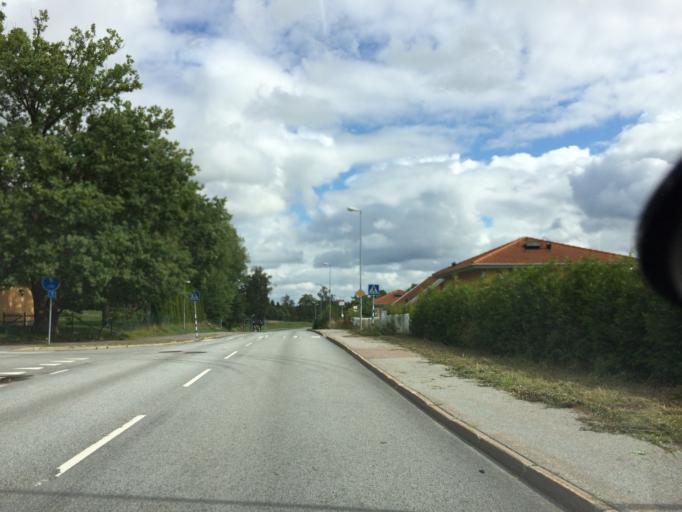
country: SE
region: Stockholm
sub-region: Upplands Vasby Kommun
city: Upplands Vaesby
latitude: 59.4618
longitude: 17.8864
